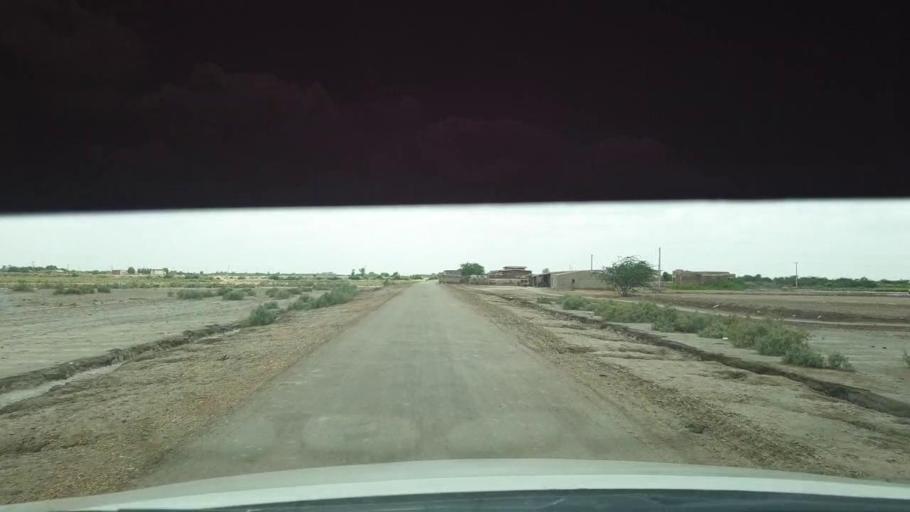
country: PK
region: Sindh
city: Kadhan
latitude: 24.5494
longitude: 69.1224
